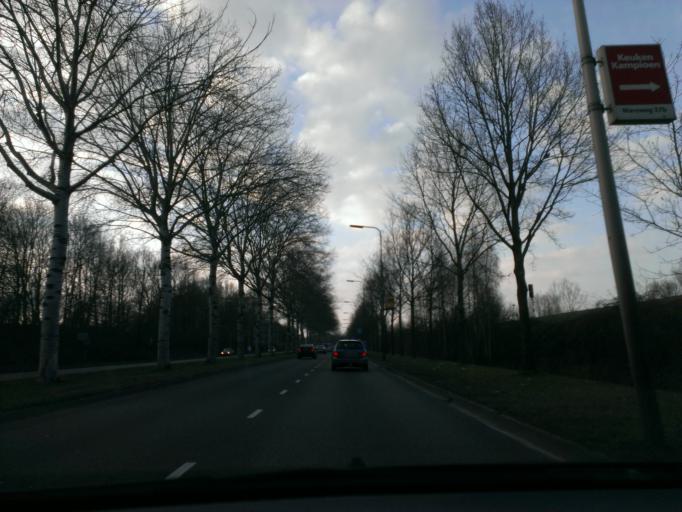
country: NL
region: Overijssel
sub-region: Gemeente Zwolle
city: Zwolle
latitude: 52.4904
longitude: 6.1205
